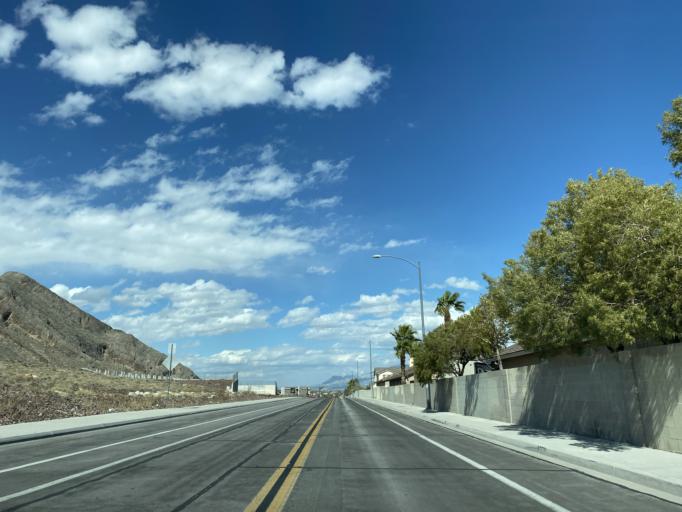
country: US
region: Nevada
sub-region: Clark County
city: Summerlin South
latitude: 36.2298
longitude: -115.3086
